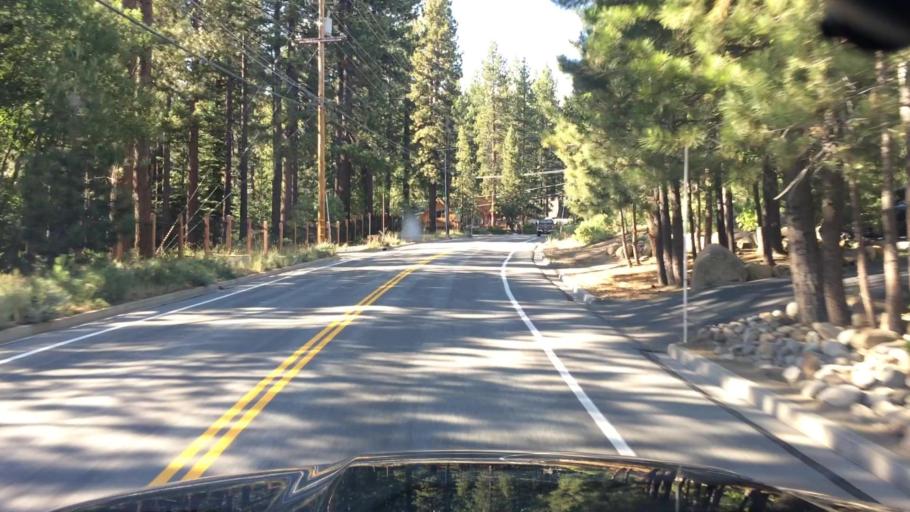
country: US
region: Nevada
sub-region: Washoe County
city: Incline Village
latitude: 39.2592
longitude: -119.9512
